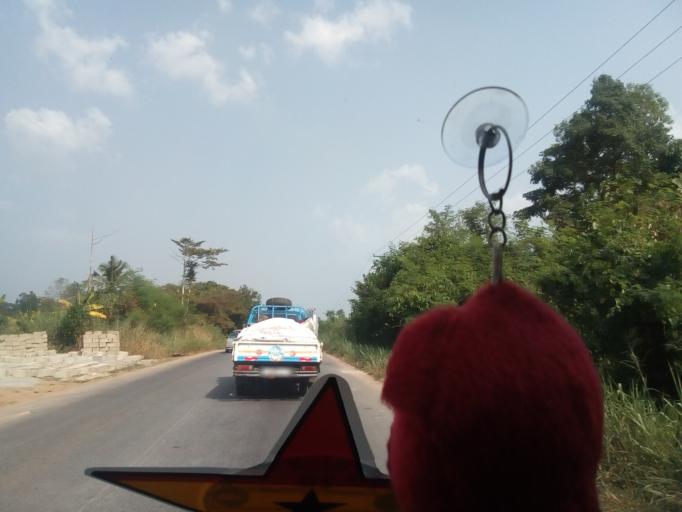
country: GH
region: Eastern
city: Suhum
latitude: 6.0443
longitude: -0.4224
